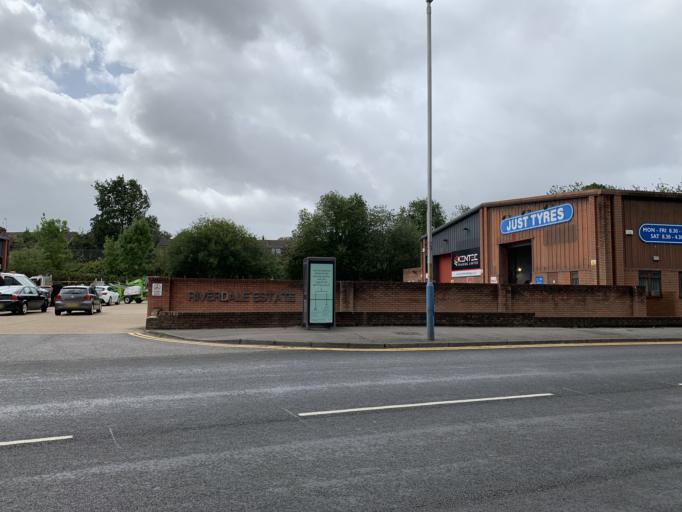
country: GB
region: England
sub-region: Kent
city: Tonbridge
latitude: 51.1907
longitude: 0.2835
